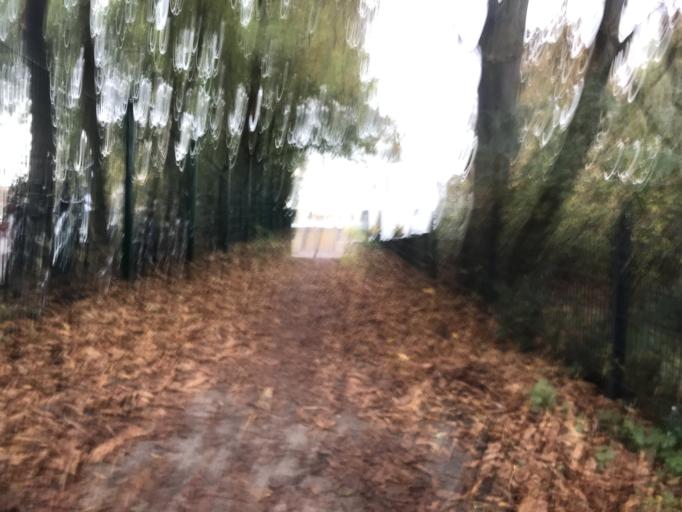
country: DE
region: North Rhine-Westphalia
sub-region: Regierungsbezirk Arnsberg
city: Hamm
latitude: 51.6905
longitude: 7.8613
